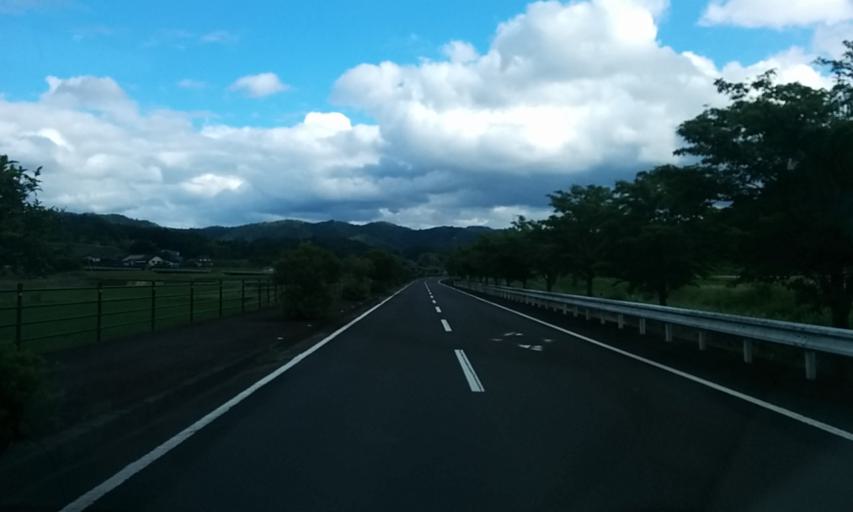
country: JP
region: Kyoto
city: Ayabe
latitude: 35.3447
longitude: 135.2889
